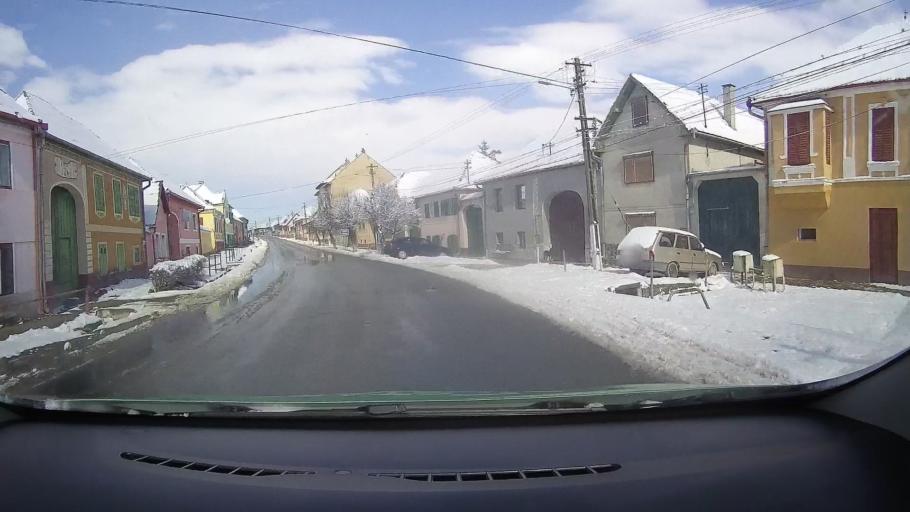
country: RO
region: Sibiu
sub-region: Comuna Altina
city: Altina
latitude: 45.9306
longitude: 24.4643
